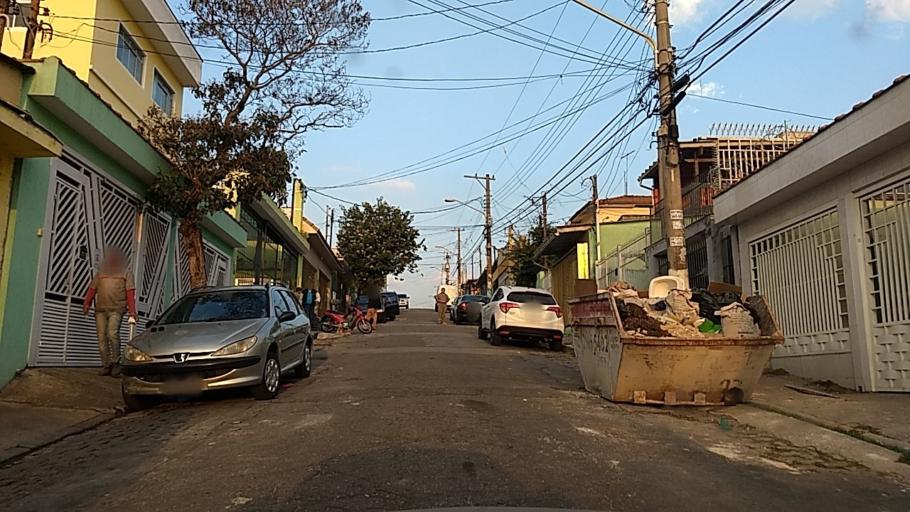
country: BR
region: Sao Paulo
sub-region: Sao Paulo
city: Sao Paulo
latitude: -23.4978
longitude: -46.5943
